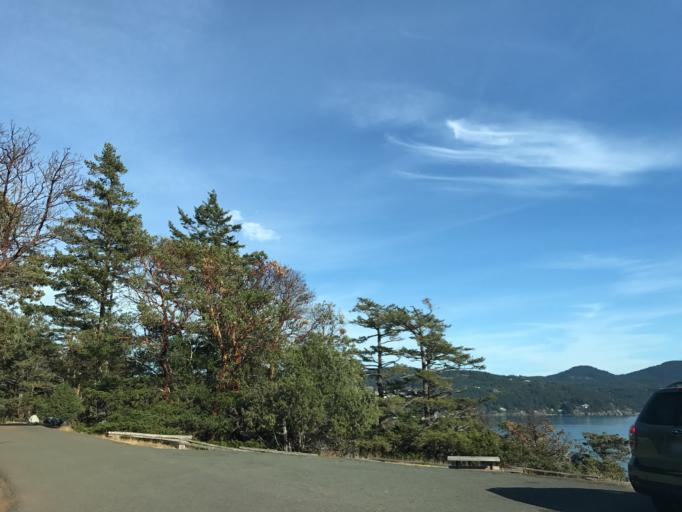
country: US
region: Washington
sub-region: Skagit County
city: Anacortes
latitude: 48.4922
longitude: -122.6929
